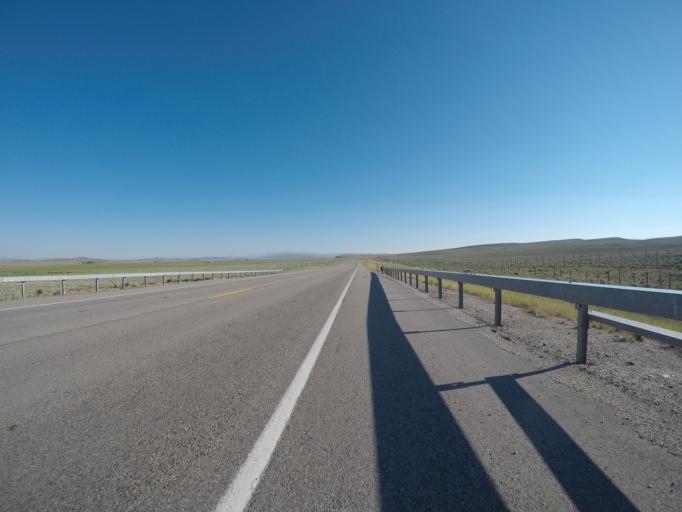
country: US
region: Wyoming
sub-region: Sublette County
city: Pinedale
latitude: 42.9257
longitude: -110.0808
